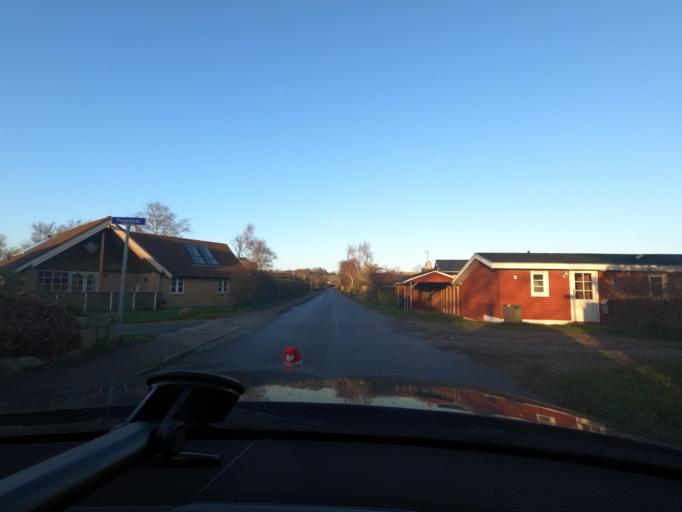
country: DK
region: South Denmark
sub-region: Sonderborg Kommune
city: Broager
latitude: 54.8988
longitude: 9.7016
